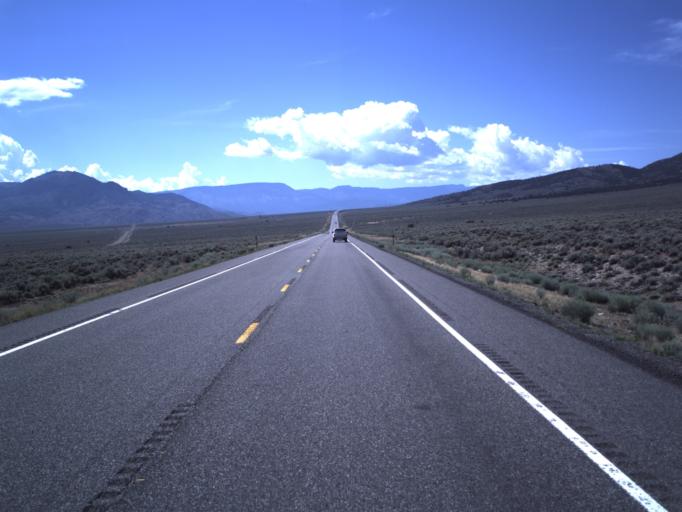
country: US
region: Utah
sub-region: Piute County
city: Junction
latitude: 38.3768
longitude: -112.2271
